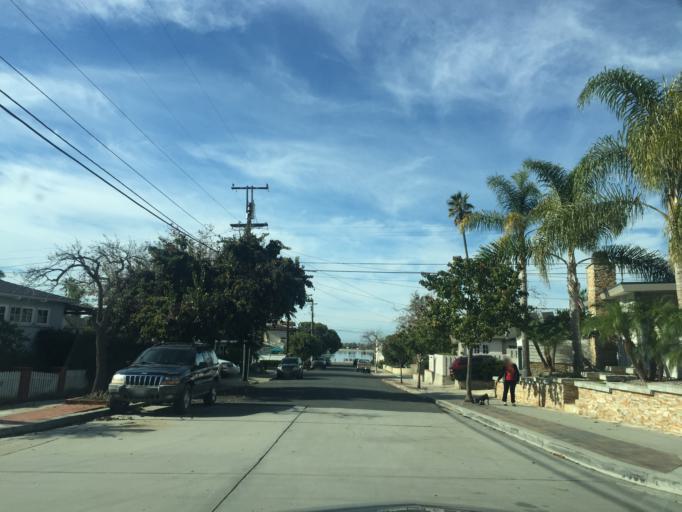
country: US
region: California
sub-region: San Diego County
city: La Jolla
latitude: 32.7846
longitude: -117.2380
